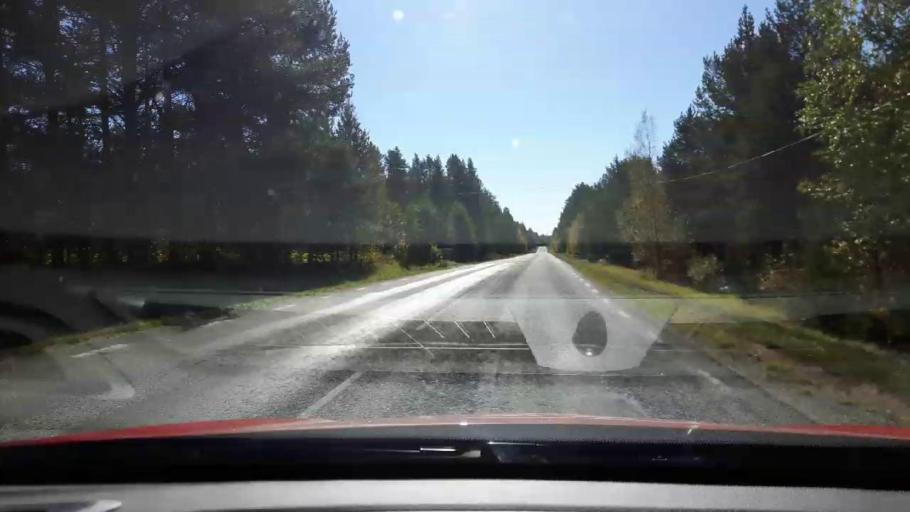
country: SE
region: Jaemtland
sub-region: Harjedalens Kommun
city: Sveg
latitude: 62.3332
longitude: 14.0551
